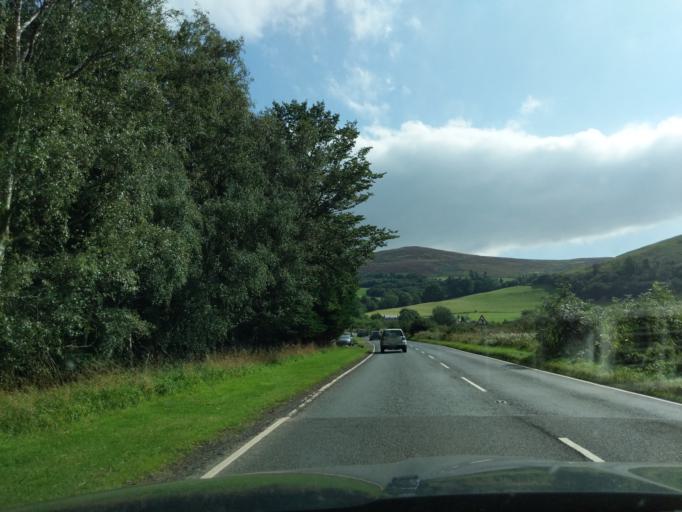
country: GB
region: England
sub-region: Northumberland
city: Wooler
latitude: 55.5637
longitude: -2.0714
